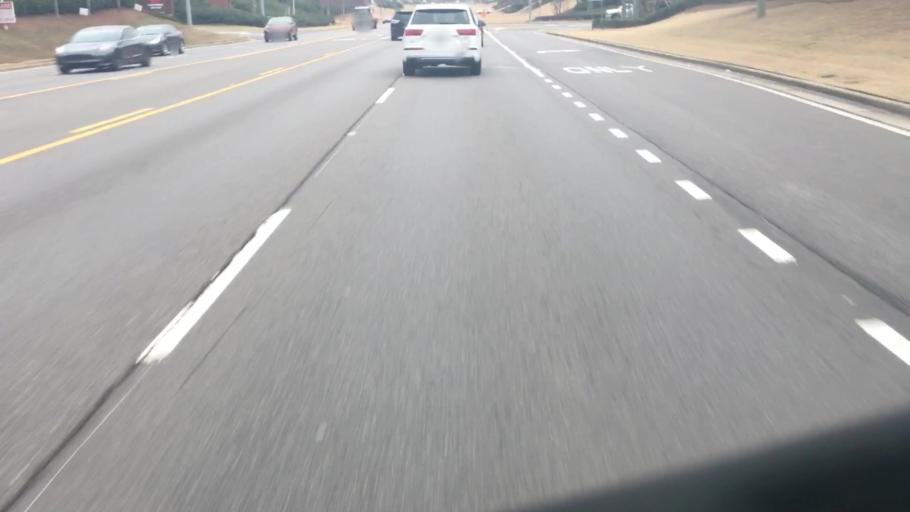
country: US
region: Alabama
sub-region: Jefferson County
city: Hoover
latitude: 33.3612
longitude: -86.8299
